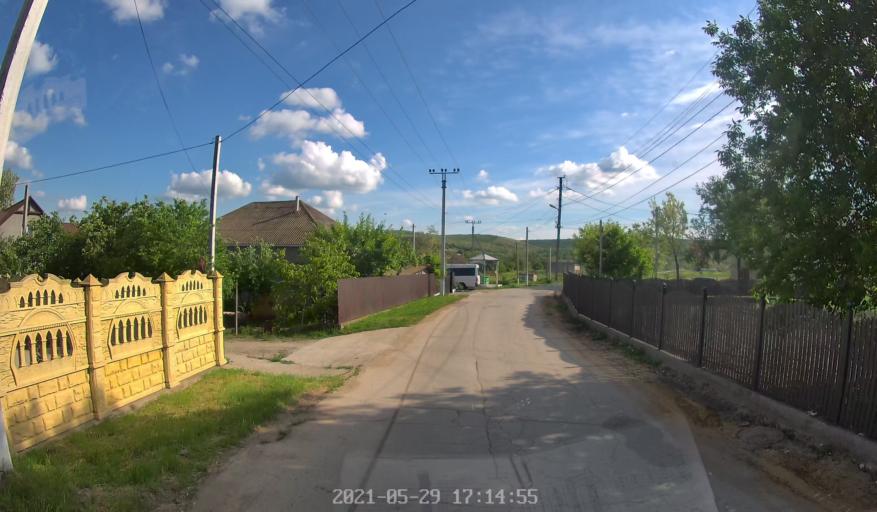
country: MD
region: Laloveni
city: Ialoveni
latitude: 46.8340
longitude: 28.8478
